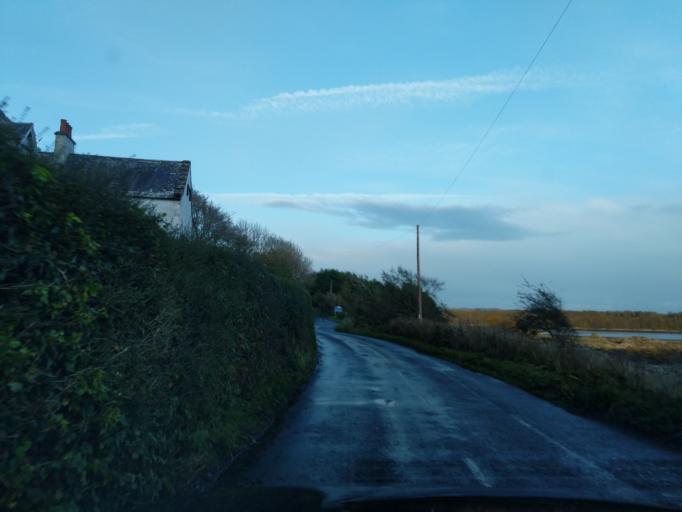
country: GB
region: Scotland
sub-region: Dumfries and Galloway
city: Kirkcudbright
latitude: 54.8161
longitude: -4.0879
